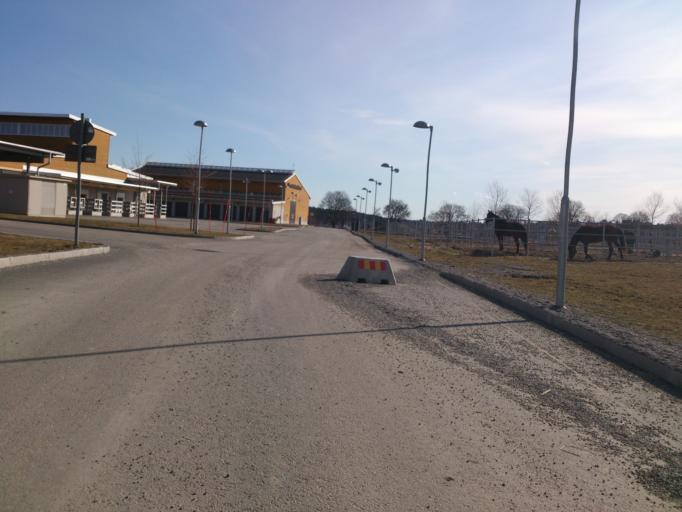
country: SE
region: Uppsala
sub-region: Uppsala Kommun
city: Uppsala
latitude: 59.8152
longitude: 17.6535
